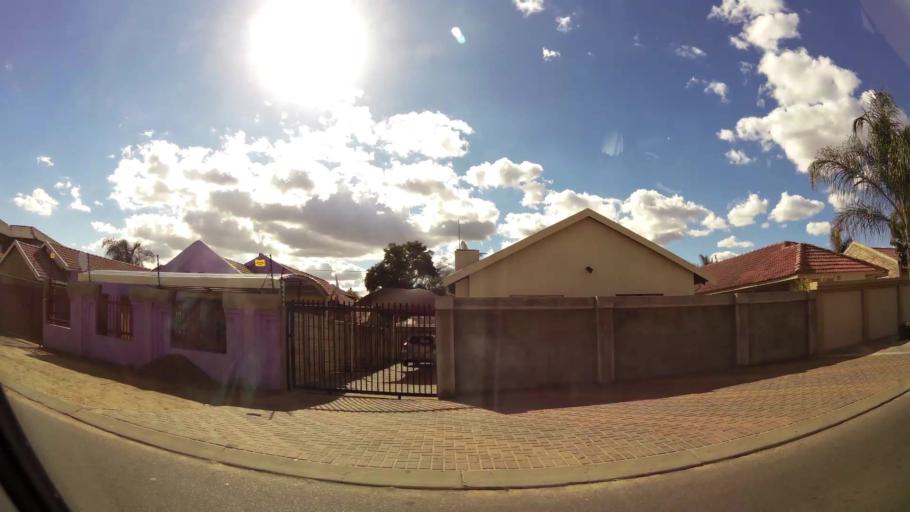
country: ZA
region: Limpopo
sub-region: Capricorn District Municipality
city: Polokwane
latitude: -23.8838
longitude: 29.4713
